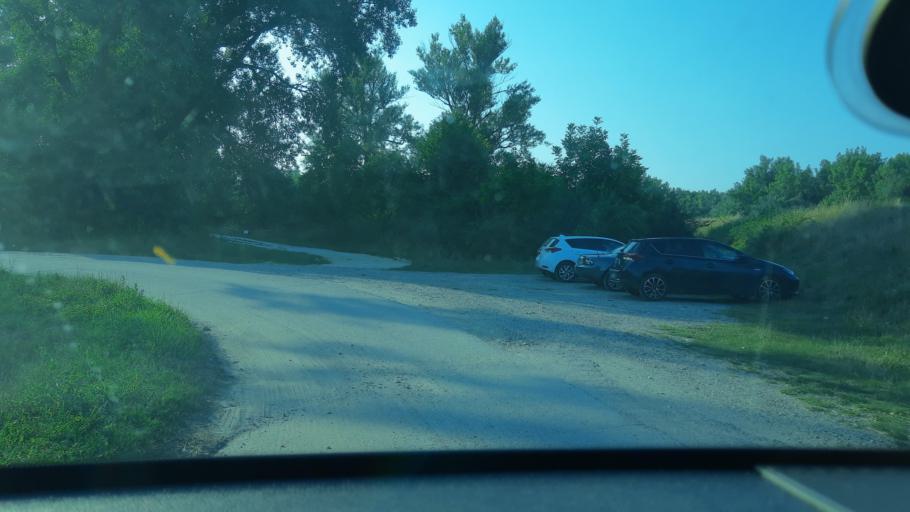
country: SK
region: Trnavsky
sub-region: Okres Trnava
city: Piestany
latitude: 48.6105
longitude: 17.8452
